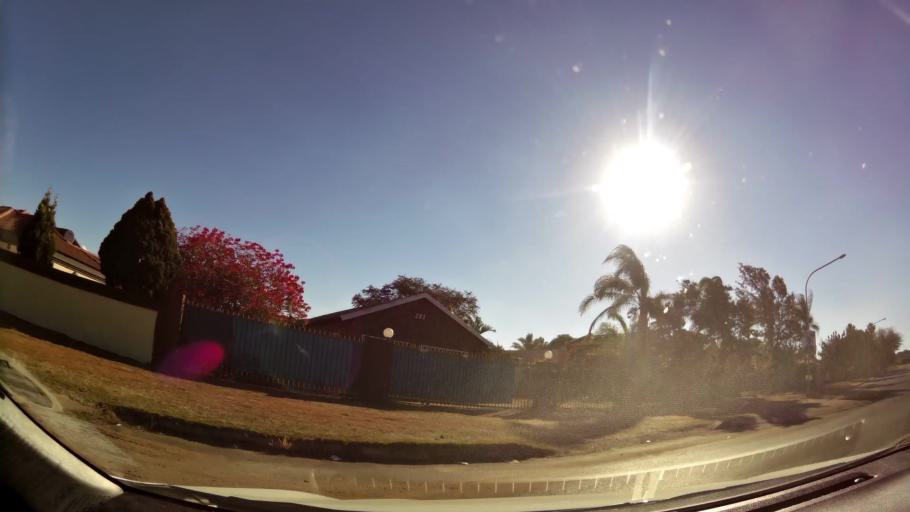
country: ZA
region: Limpopo
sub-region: Capricorn District Municipality
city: Polokwane
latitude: -23.9027
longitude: 29.4989
